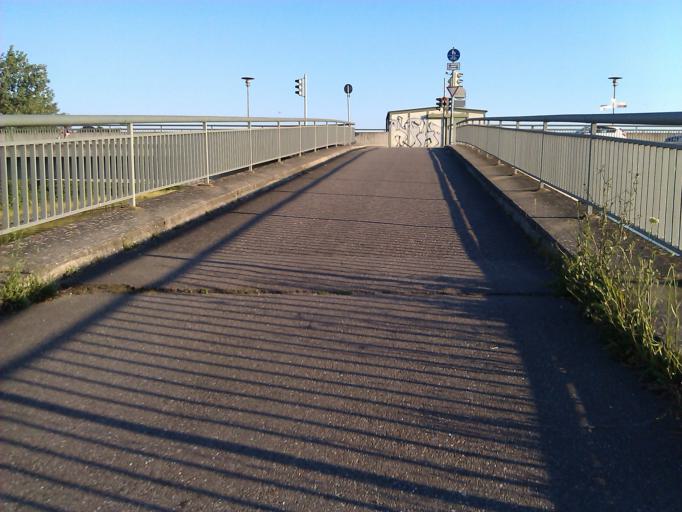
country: DE
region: Baden-Wuerttemberg
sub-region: Regierungsbezirk Stuttgart
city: Neckarsulm
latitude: 49.1898
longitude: 9.2166
